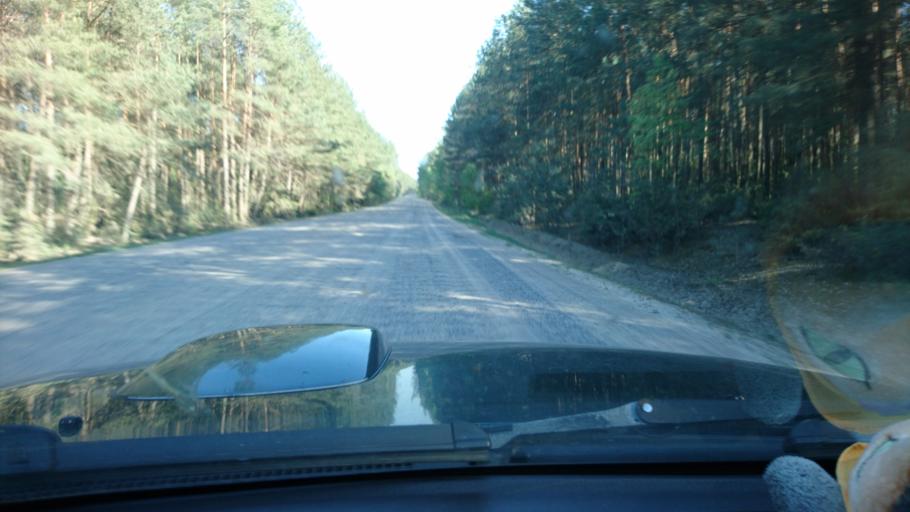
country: BY
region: Brest
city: Zhabinka
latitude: 52.3853
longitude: 24.1109
